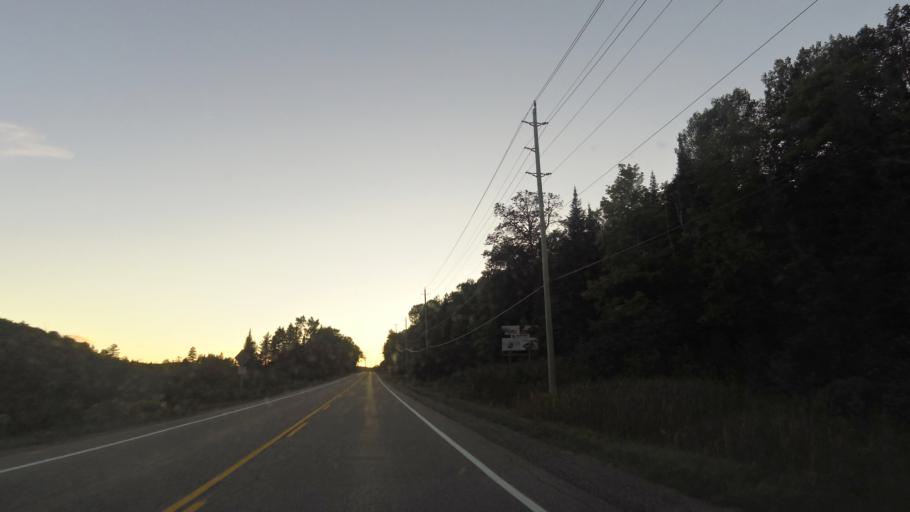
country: CA
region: Ontario
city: Bancroft
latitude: 45.0217
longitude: -78.3570
